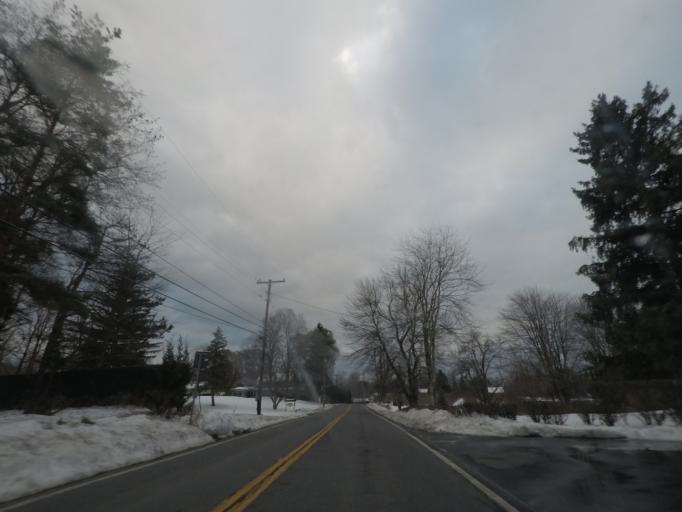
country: US
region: New York
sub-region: Ulster County
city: Clintondale
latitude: 41.6785
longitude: -74.1039
